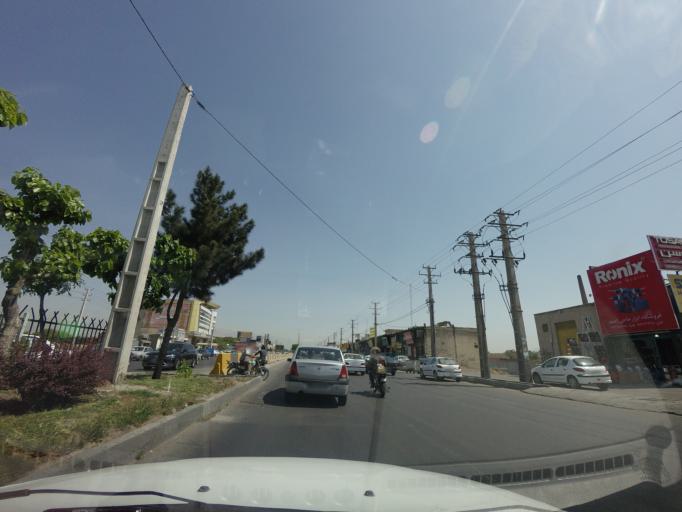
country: IR
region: Tehran
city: Eslamshahr
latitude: 35.6011
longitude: 51.3005
